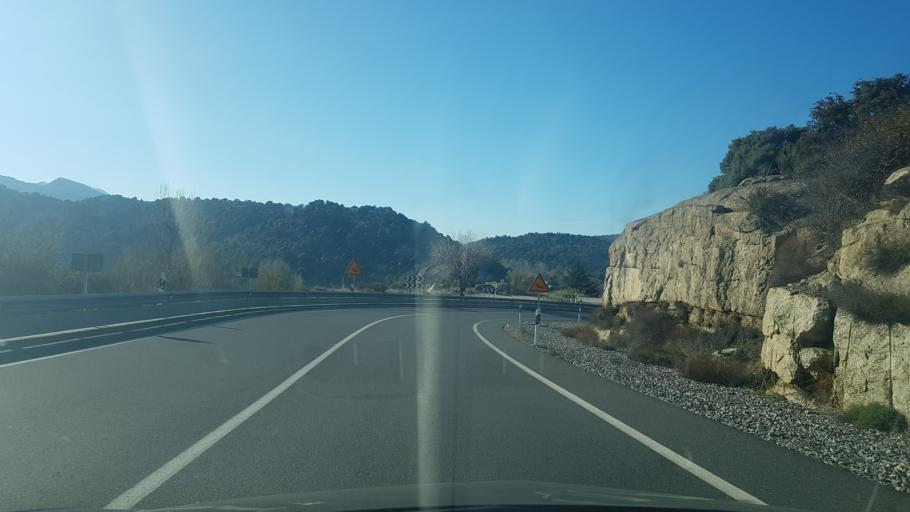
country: ES
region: Castille and Leon
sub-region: Provincia de Avila
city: El Tiemblo
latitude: 40.4379
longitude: -4.5606
